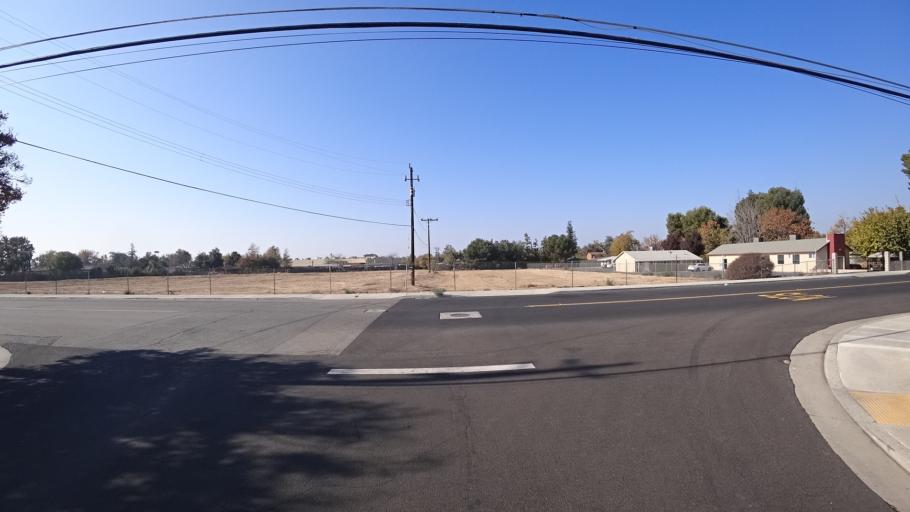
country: US
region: California
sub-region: Kern County
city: Bakersfield
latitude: 35.3431
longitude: -119.0343
